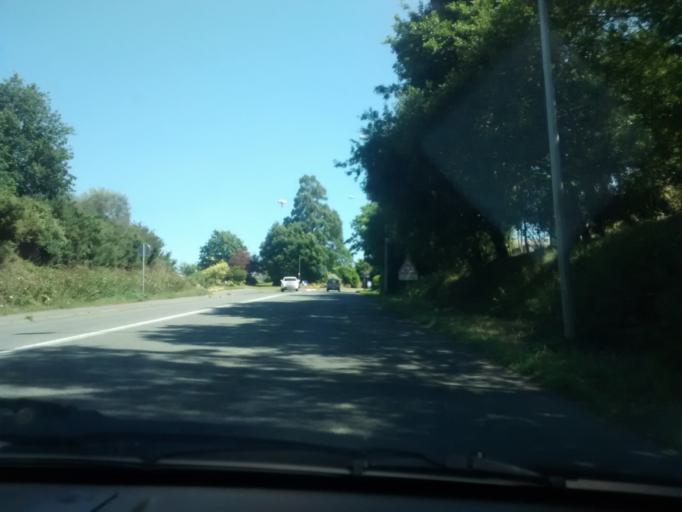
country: FR
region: Brittany
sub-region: Departement des Cotes-d'Armor
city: Lannion
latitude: 48.7259
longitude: -3.4423
